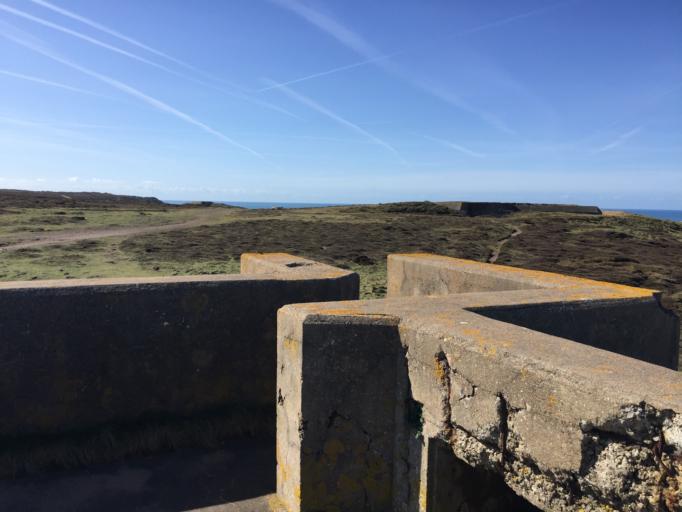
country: JE
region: St Helier
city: Saint Helier
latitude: 49.2526
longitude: -2.2516
